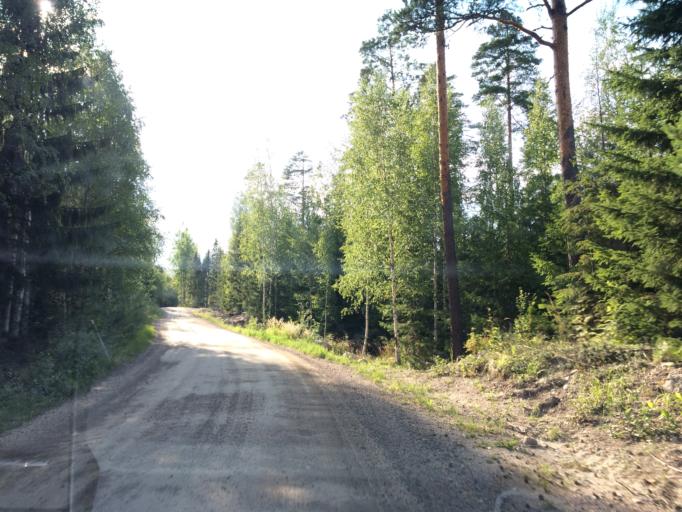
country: FI
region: Haeme
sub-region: Haemeenlinna
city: Haemeenlinna
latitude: 60.9423
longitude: 24.3789
